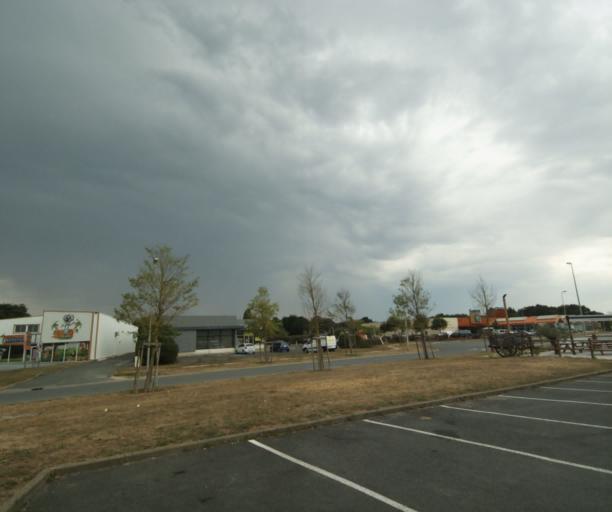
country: FR
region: Poitou-Charentes
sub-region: Departement de la Charente-Maritime
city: Tonnay-Charente
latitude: 45.9524
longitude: -0.8966
